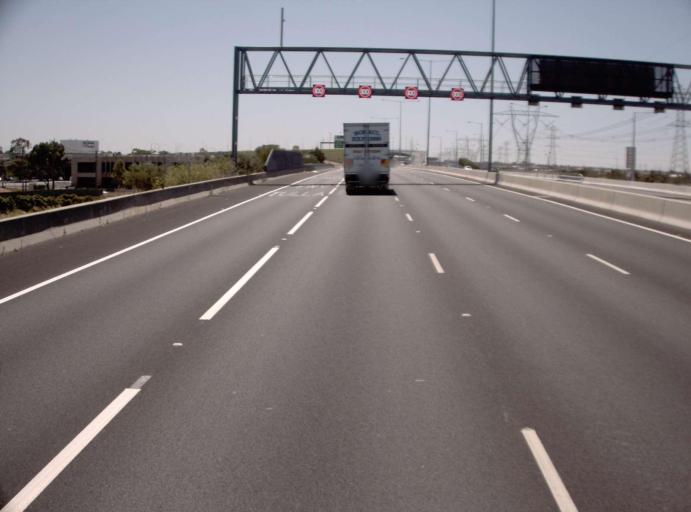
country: AU
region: Victoria
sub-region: Moreland
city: Gowanbrae
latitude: -37.7087
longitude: 144.8845
